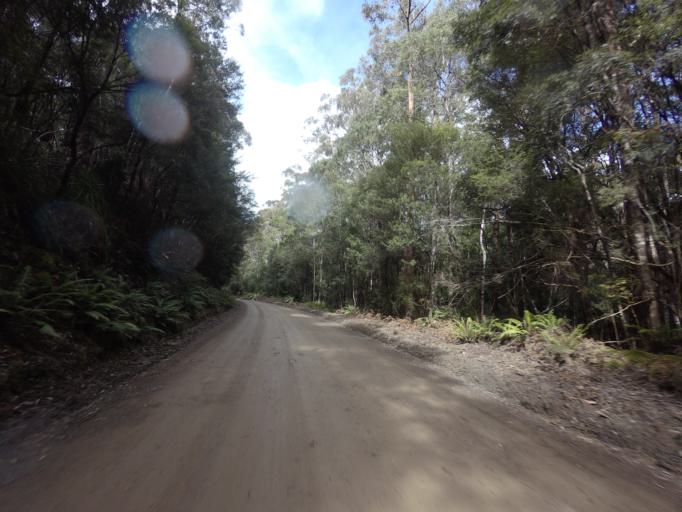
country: AU
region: Tasmania
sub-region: Huon Valley
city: Geeveston
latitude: -43.3913
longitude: 146.8537
